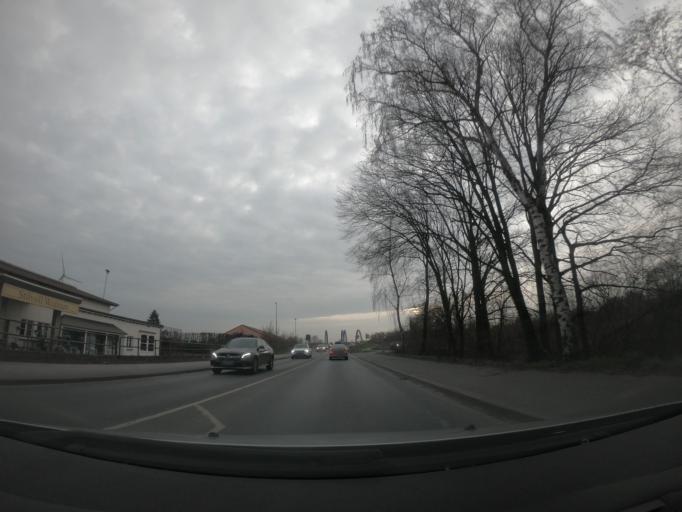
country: DE
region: North Rhine-Westphalia
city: Lunen
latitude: 51.6041
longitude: 7.4937
